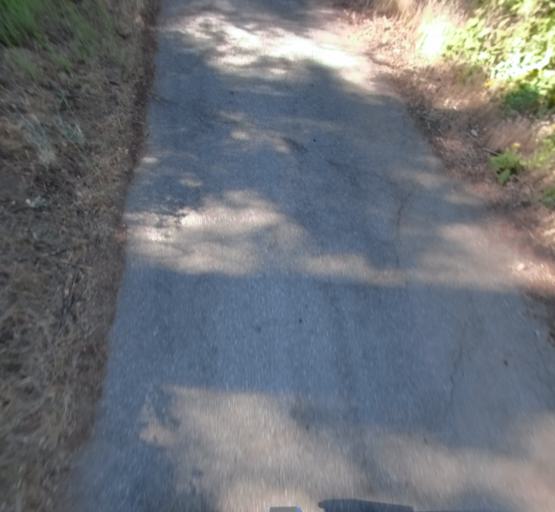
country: US
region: California
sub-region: Madera County
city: Oakhurst
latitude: 37.3978
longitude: -119.6255
